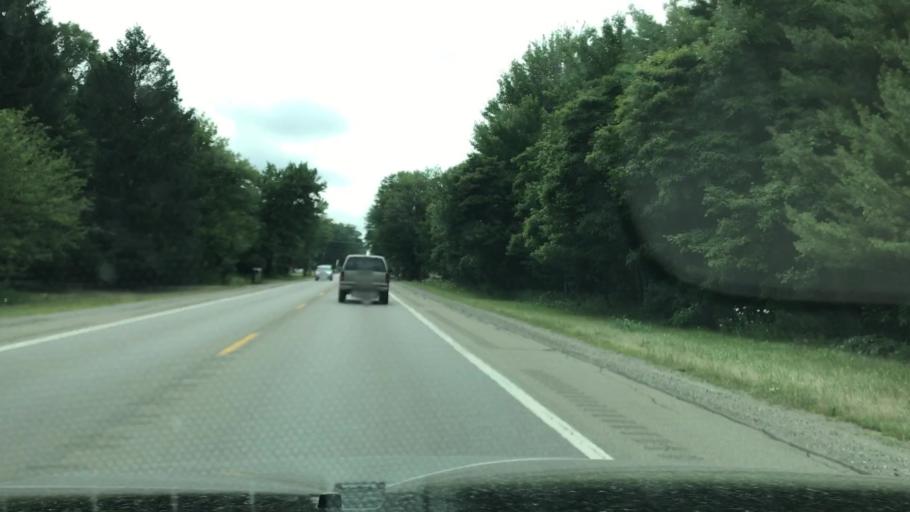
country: US
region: Michigan
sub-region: Muskegon County
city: Fruitport
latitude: 43.0739
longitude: -86.1238
